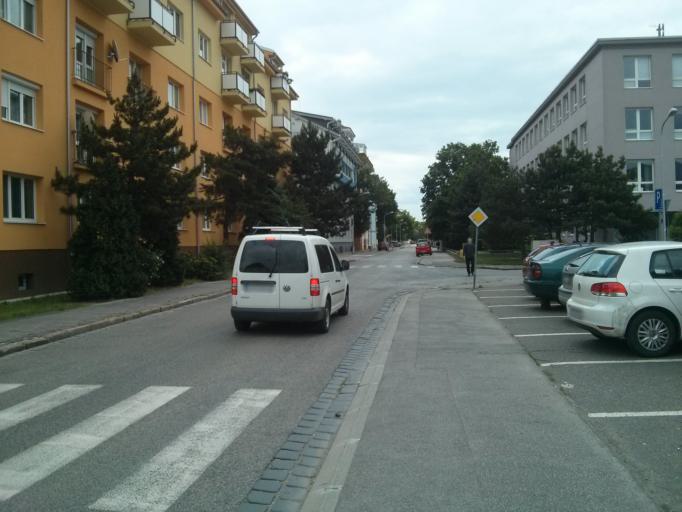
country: SK
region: Bratislavsky
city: Bratislava
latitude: 48.1743
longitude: 17.1356
